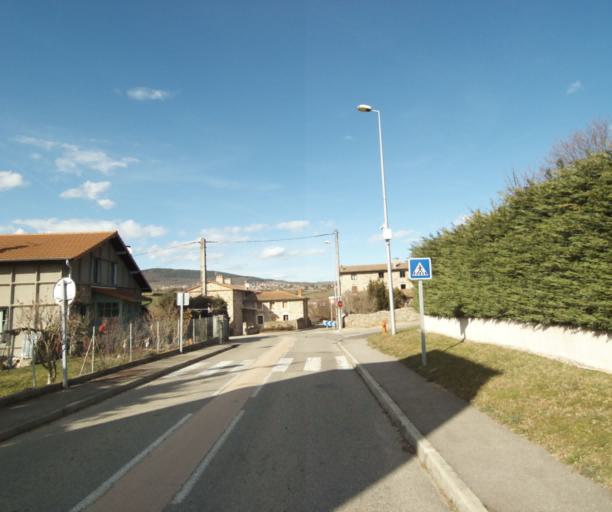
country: FR
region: Rhone-Alpes
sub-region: Departement de l'Ardeche
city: Boulieu-les-Annonay
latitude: 45.2585
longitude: 4.6858
